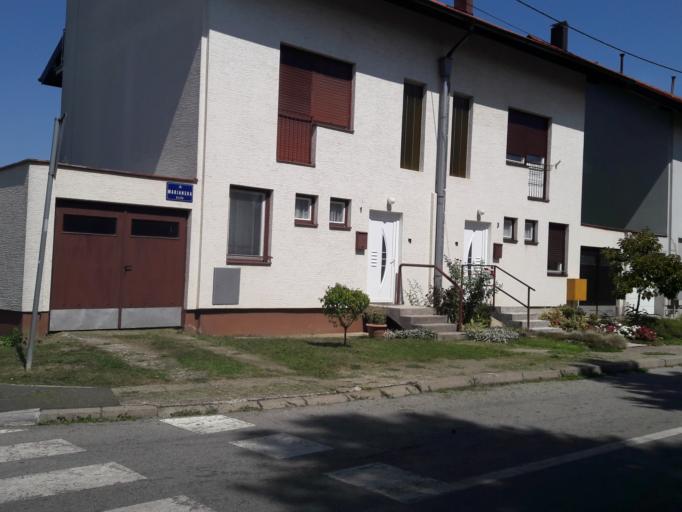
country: HR
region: Osjecko-Baranjska
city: Visnjevac
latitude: 45.5597
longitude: 18.6422
